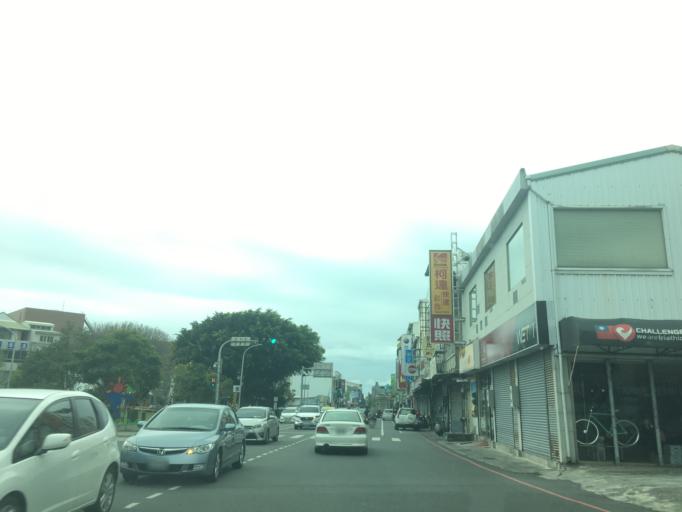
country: TW
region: Taiwan
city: Taitung City
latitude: 22.7573
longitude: 121.1429
